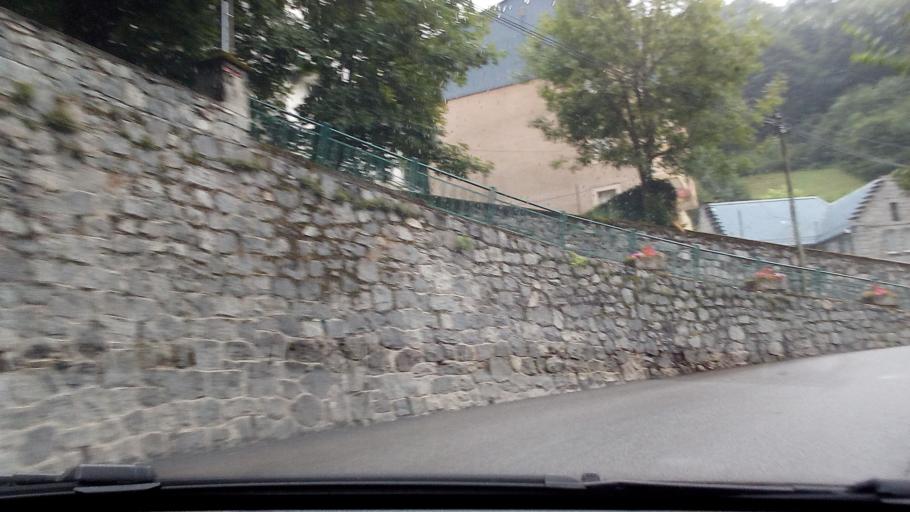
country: FR
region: Midi-Pyrenees
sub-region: Departement des Hautes-Pyrenees
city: Luz-Saint-Sauveur
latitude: 42.8956
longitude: 0.0591
